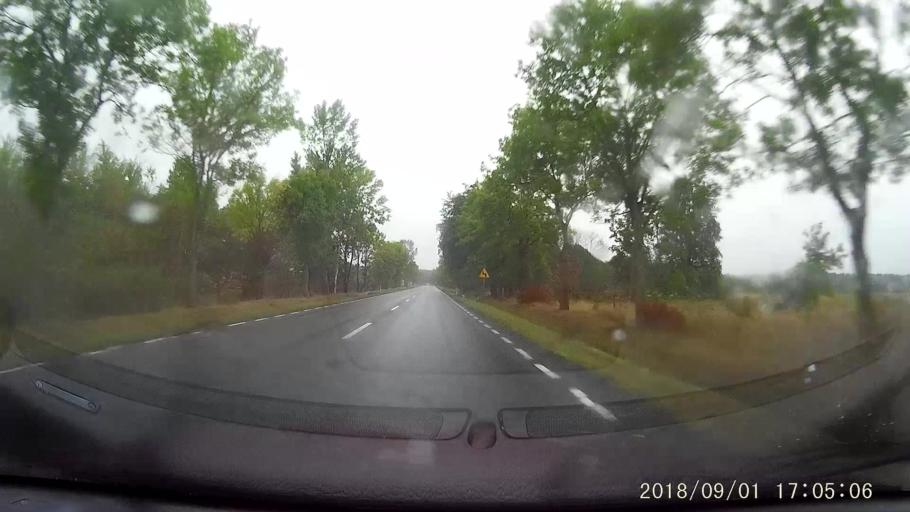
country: PL
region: Lubusz
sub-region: Powiat zielonogorski
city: Swidnica
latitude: 51.8571
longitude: 15.3559
